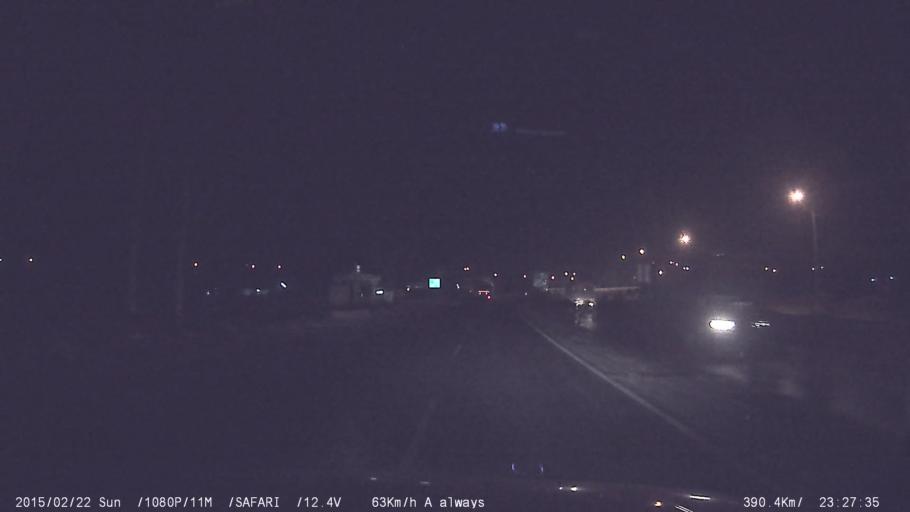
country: IN
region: Tamil Nadu
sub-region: Salem
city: Salem
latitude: 11.6376
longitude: 78.1214
